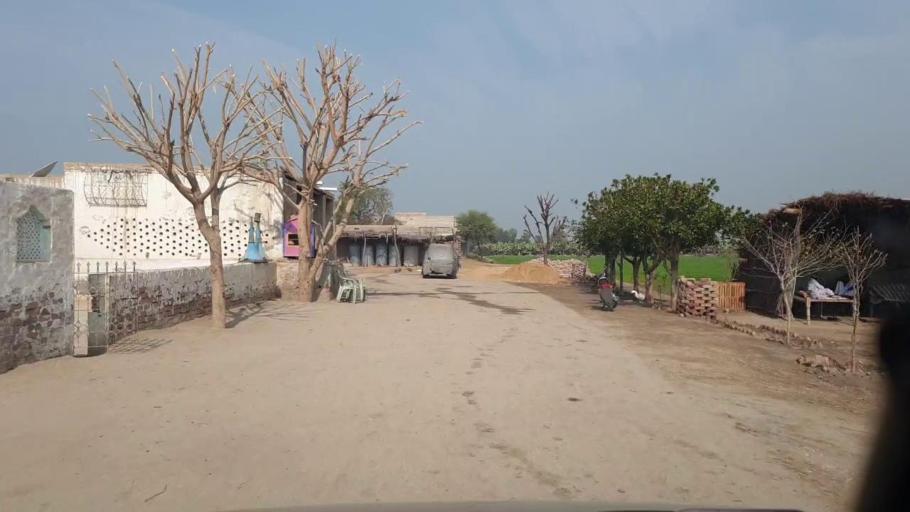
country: PK
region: Sindh
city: Shahdadpur
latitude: 26.0129
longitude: 68.5101
